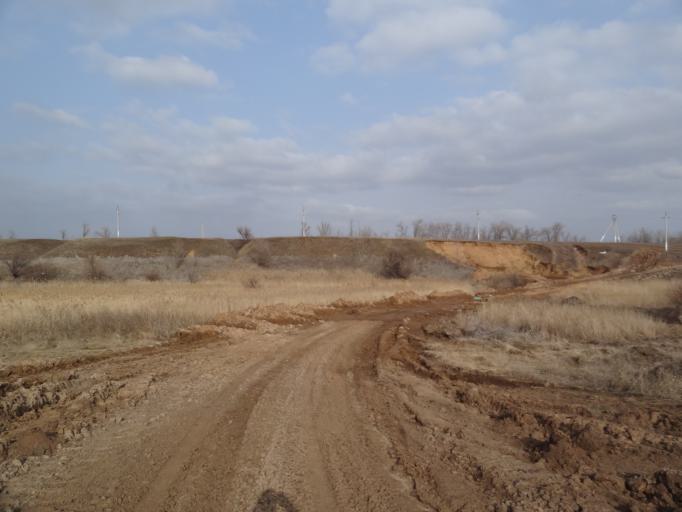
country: RU
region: Saratov
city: Shumeyka
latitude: 51.4879
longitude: 46.2802
